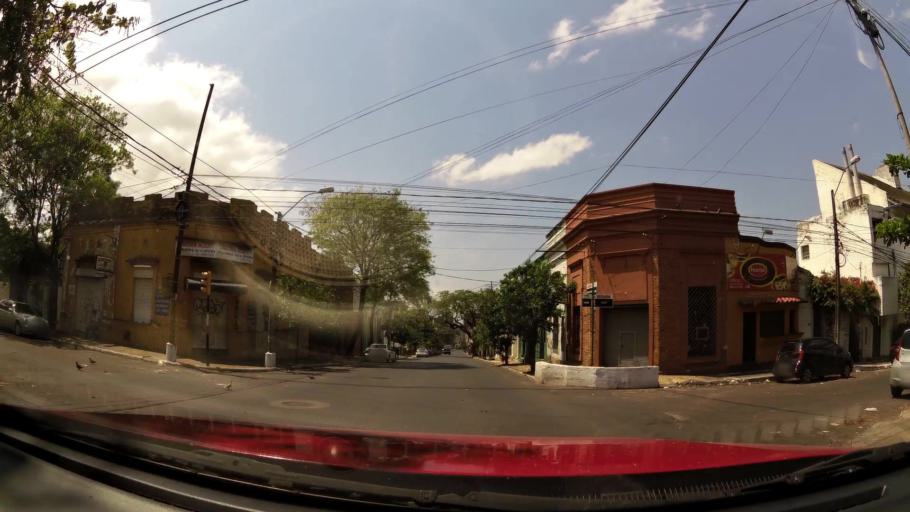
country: PY
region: Asuncion
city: Asuncion
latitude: -25.2862
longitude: -57.6449
